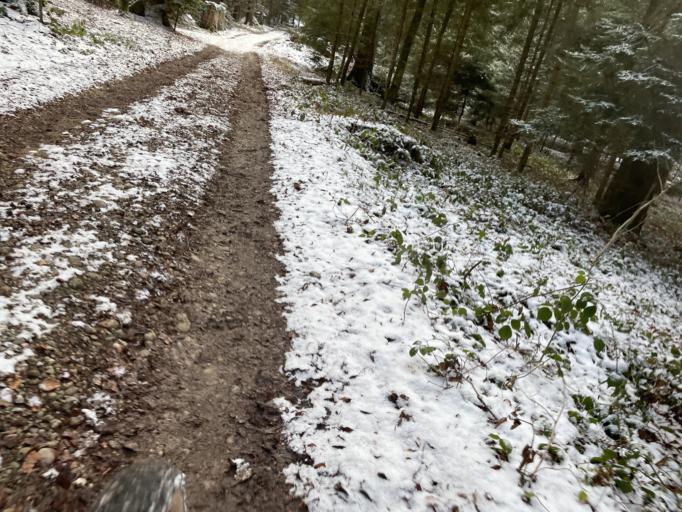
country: CH
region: Lucerne
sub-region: Entlebuch District
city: Oberdiessbach
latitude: 46.8487
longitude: 7.6086
